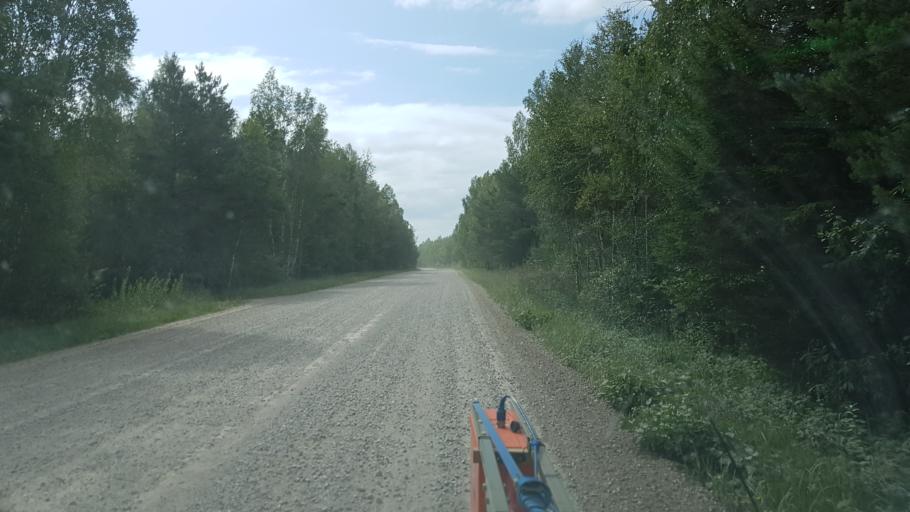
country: EE
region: Paernumaa
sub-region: Audru vald
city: Audru
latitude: 58.5233
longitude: 24.4066
